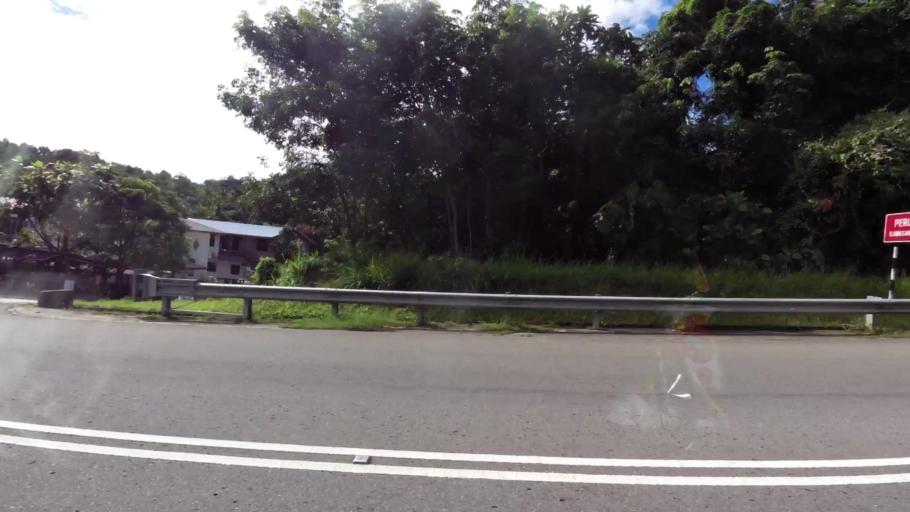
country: BN
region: Brunei and Muara
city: Bandar Seri Begawan
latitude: 4.9008
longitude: 114.9744
